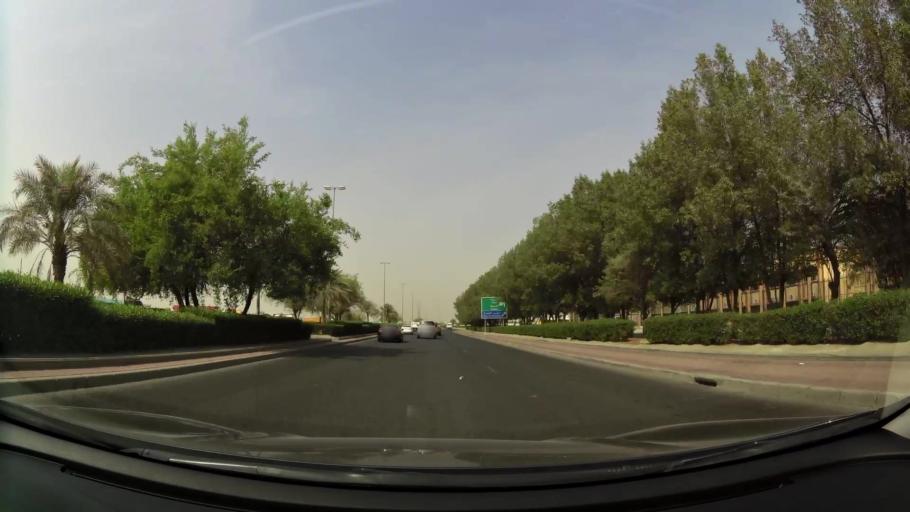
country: KW
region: Al Asimah
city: Ar Rabiyah
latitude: 29.2592
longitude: 47.9146
